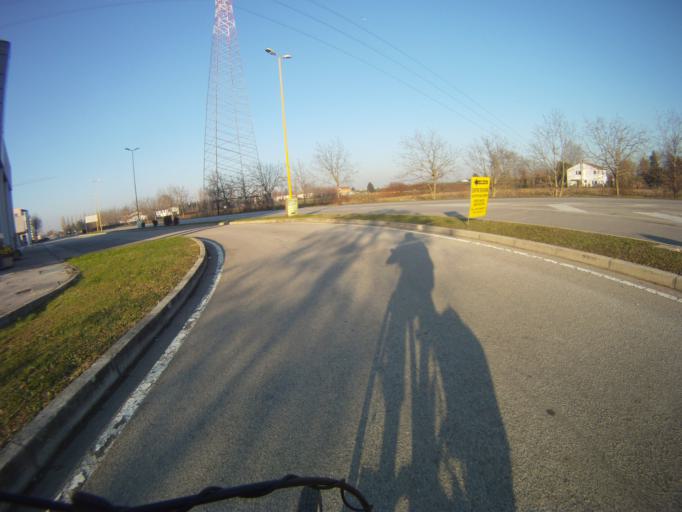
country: IT
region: Veneto
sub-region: Provincia di Padova
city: Ponte San Nicolo
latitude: 45.3557
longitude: 11.9316
